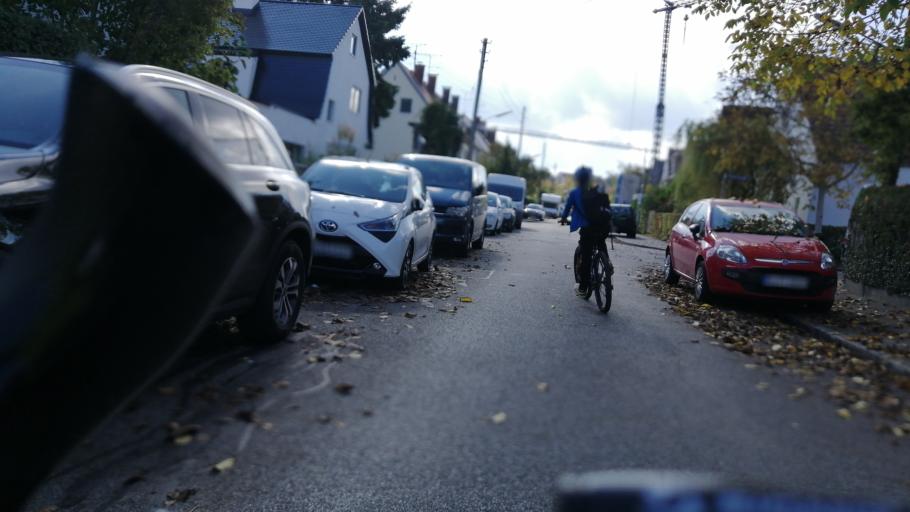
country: DE
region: Bavaria
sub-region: Upper Bavaria
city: Pasing
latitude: 48.1317
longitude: 11.4937
